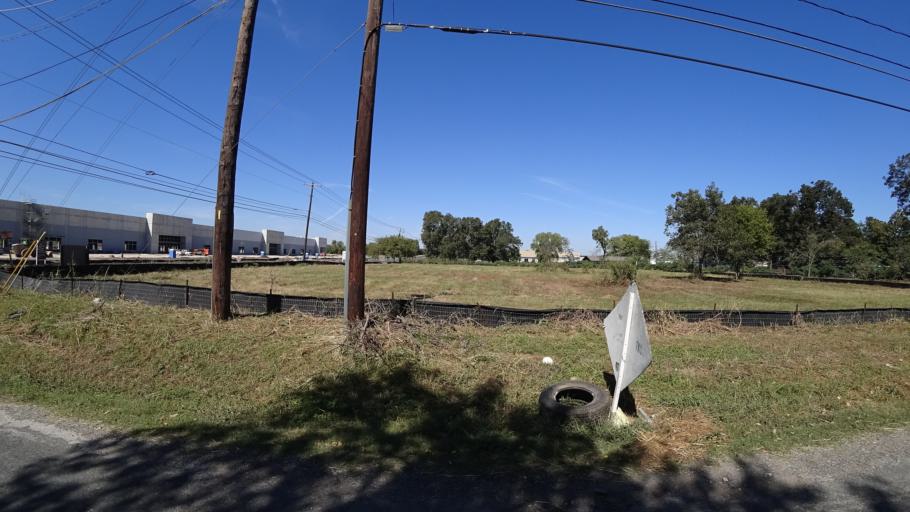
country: US
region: Texas
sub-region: Travis County
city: Austin
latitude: 30.1854
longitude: -97.6904
